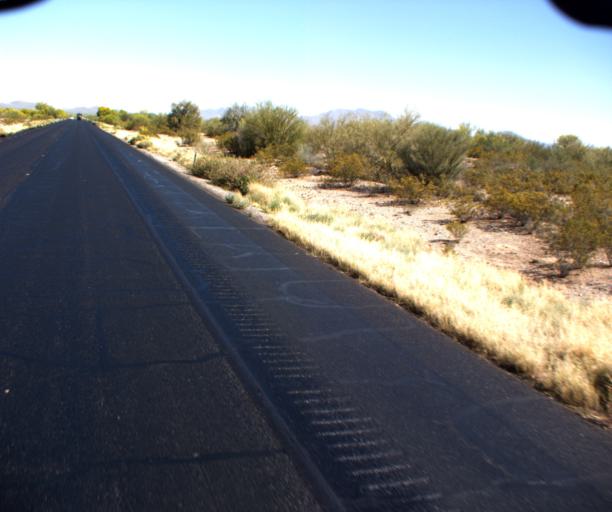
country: US
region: Arizona
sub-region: Pinal County
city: Maricopa
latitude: 32.8464
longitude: -112.2930
